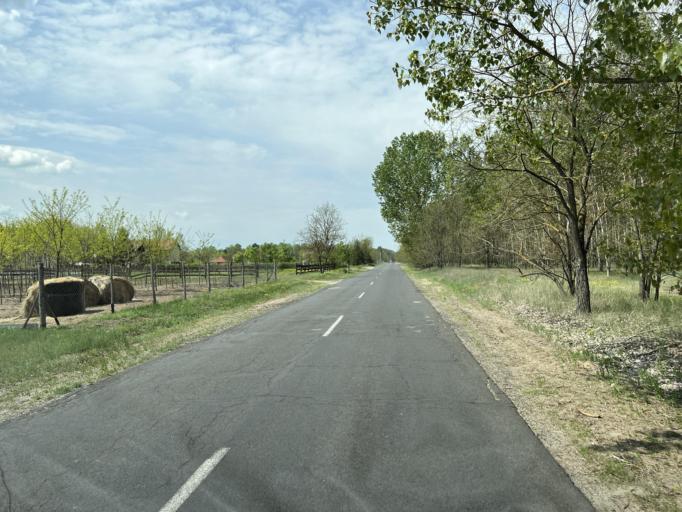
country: HU
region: Pest
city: Csemo
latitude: 47.1244
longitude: 19.6832
